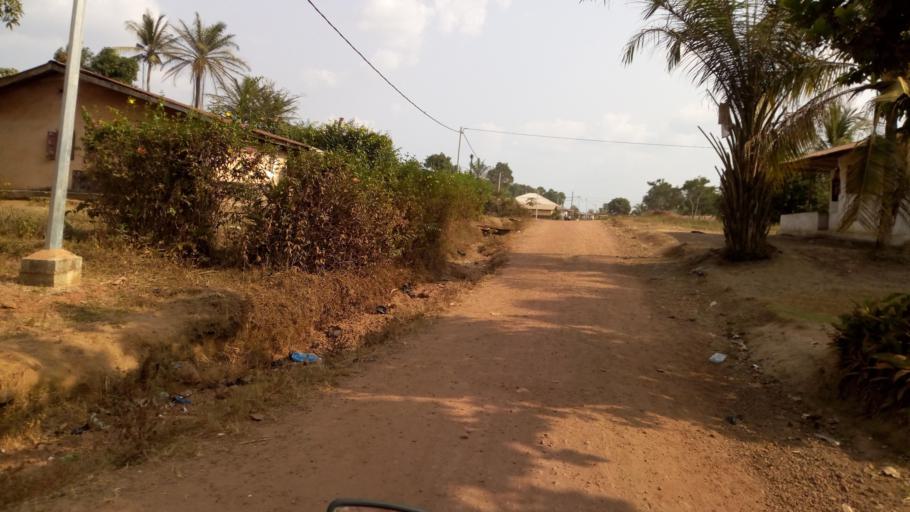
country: SL
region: Southern Province
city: Mogbwemo
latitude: 7.7624
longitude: -12.3098
